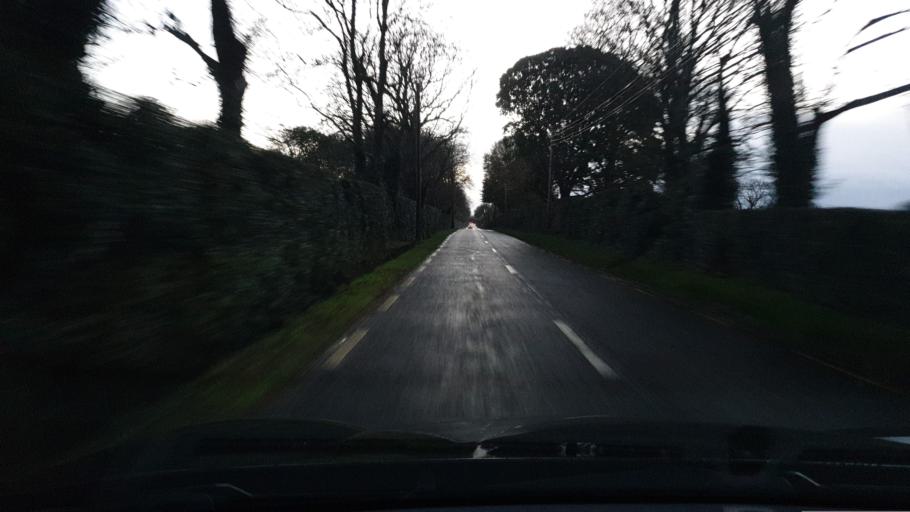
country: IE
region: Leinster
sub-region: Kildare
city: Maynooth
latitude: 53.3612
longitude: -6.6291
